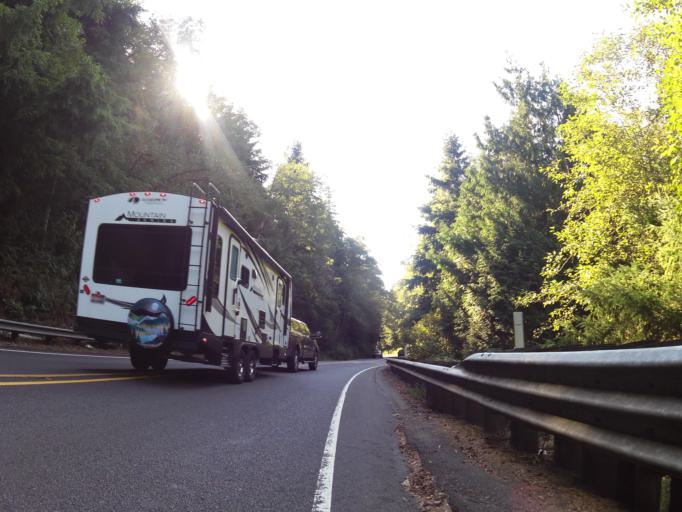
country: US
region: Oregon
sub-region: Clatsop County
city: Cannon Beach
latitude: 45.7565
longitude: -123.9596
